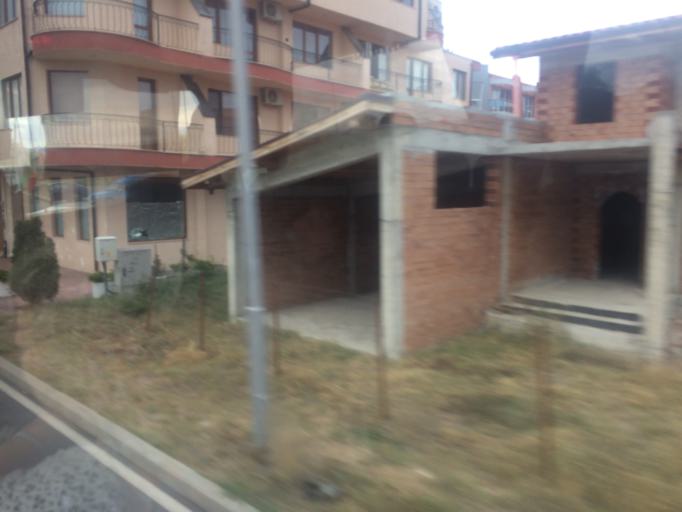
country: BG
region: Burgas
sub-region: Obshtina Nesebur
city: Ravda
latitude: 42.6590
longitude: 27.7022
